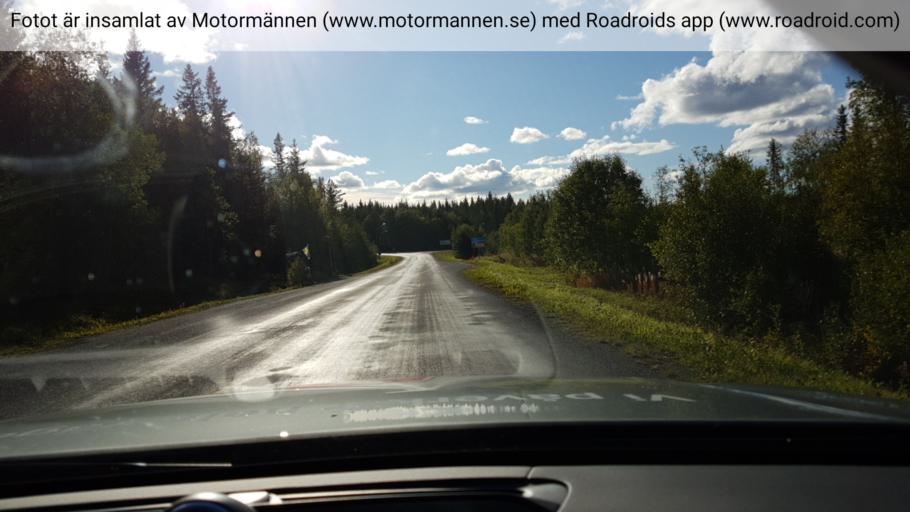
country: SE
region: Jaemtland
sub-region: Krokoms Kommun
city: Valla
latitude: 63.1846
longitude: 14.0189
